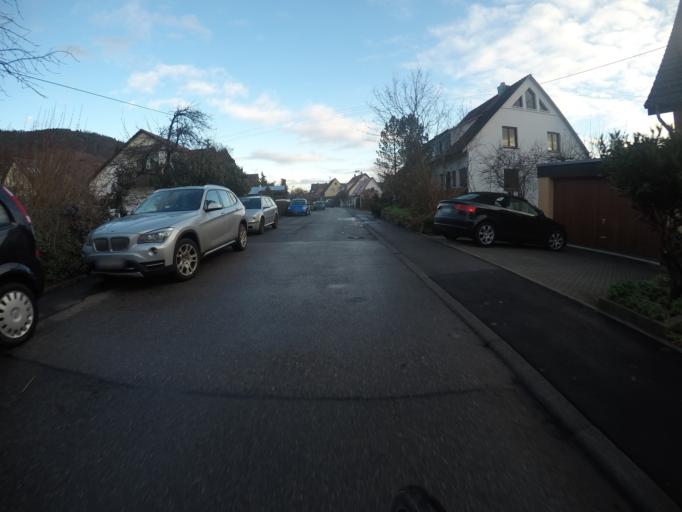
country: DE
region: Baden-Wuerttemberg
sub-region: Tuebingen Region
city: Tuebingen
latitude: 48.5026
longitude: 8.9958
